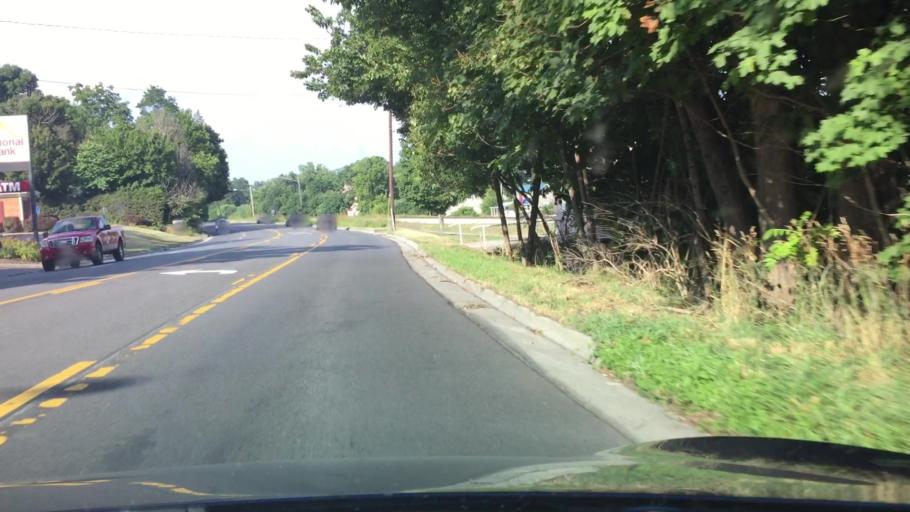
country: US
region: Virginia
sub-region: Pulaski County
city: Dublin
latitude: 37.1062
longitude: -80.6848
